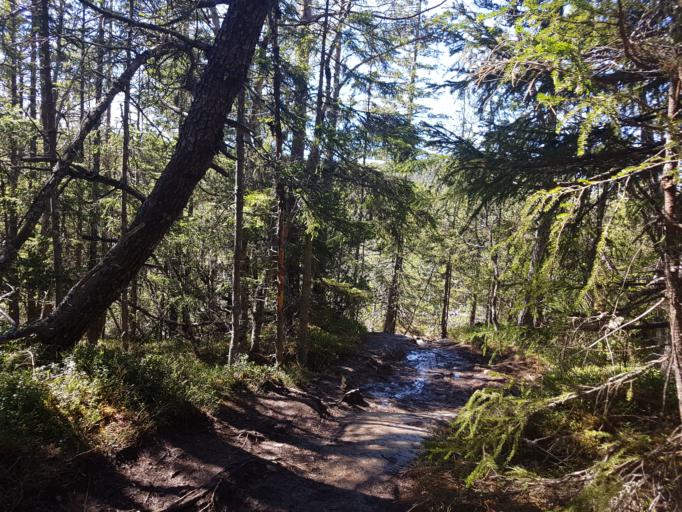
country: NO
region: Sor-Trondelag
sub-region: Trondheim
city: Trondheim
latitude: 63.4349
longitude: 10.3217
